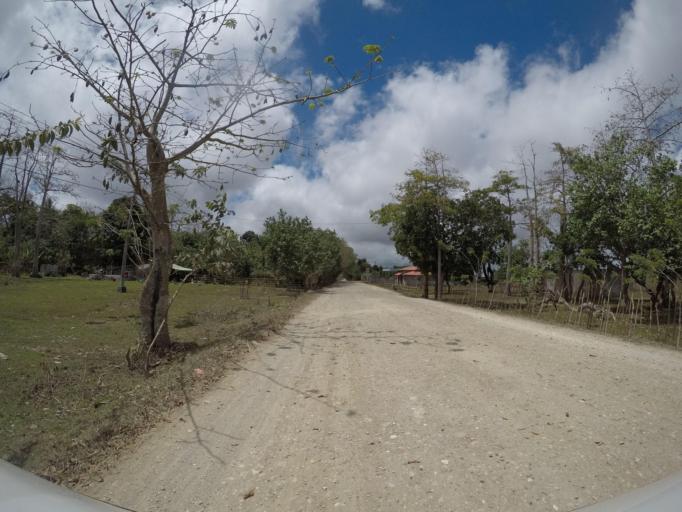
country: TL
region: Lautem
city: Lospalos
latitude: -8.4396
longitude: 126.9820
